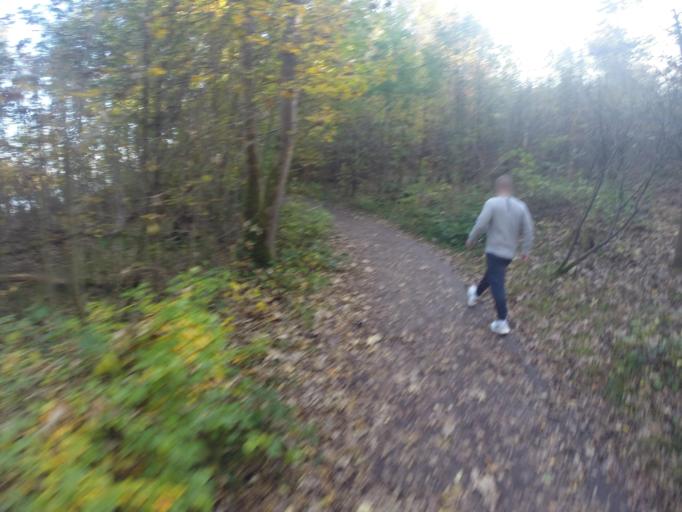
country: DK
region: Capital Region
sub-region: Fureso Kommune
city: Stavnsholt
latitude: 55.7768
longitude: 12.4365
